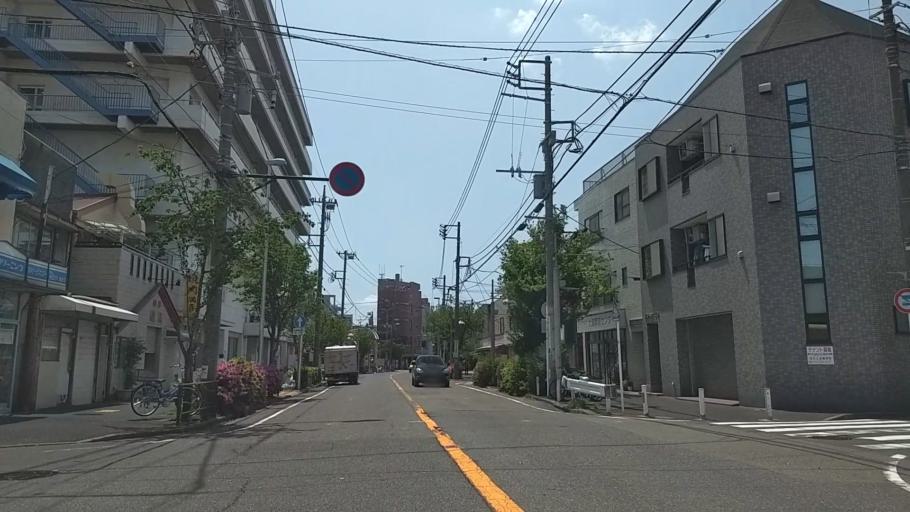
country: JP
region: Kanagawa
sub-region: Kawasaki-shi
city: Kawasaki
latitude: 35.5227
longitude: 139.7218
